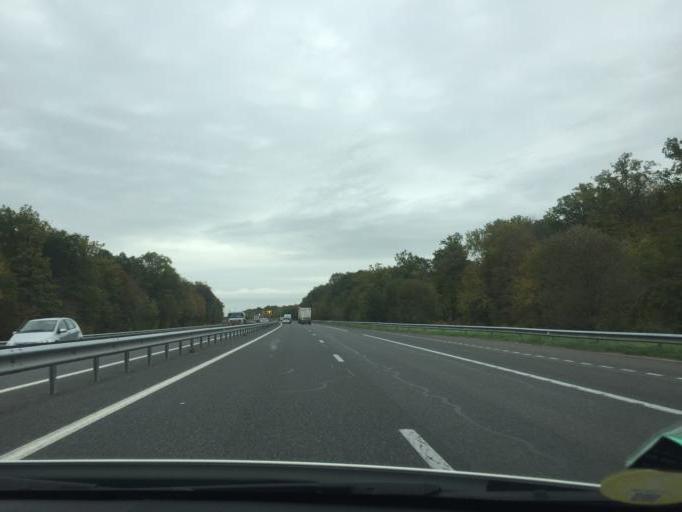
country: FR
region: Bourgogne
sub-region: Departement de l'Yonne
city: Egriselles-le-Bocage
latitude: 48.1234
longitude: 3.1415
